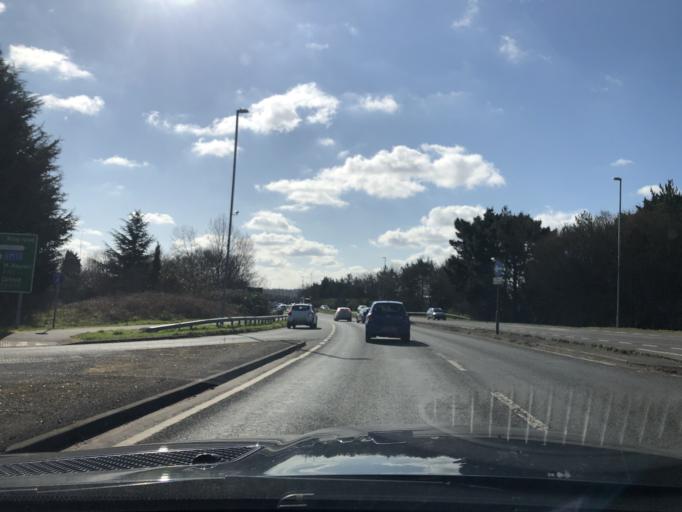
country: GB
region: England
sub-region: Northamptonshire
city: Northampton
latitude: 52.2476
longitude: -0.8379
